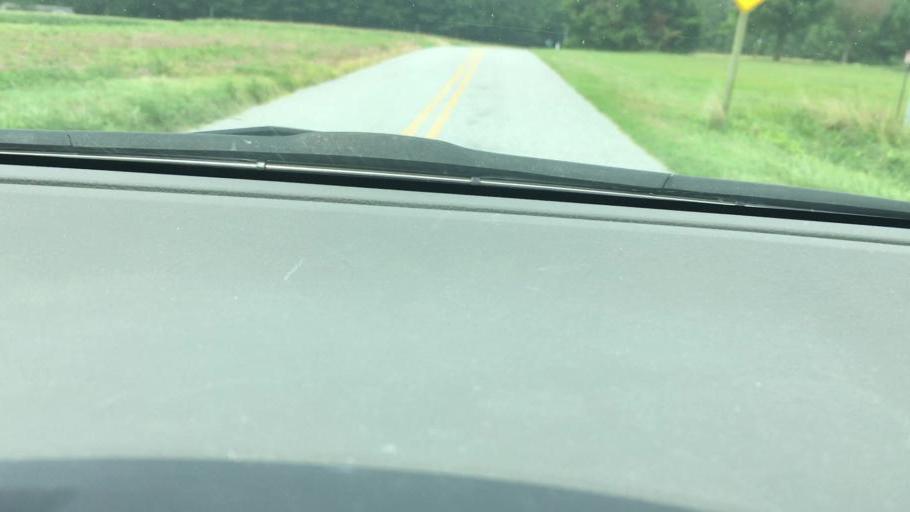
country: US
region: Maryland
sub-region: Worcester County
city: Pocomoke City
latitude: 38.0629
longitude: -75.5048
